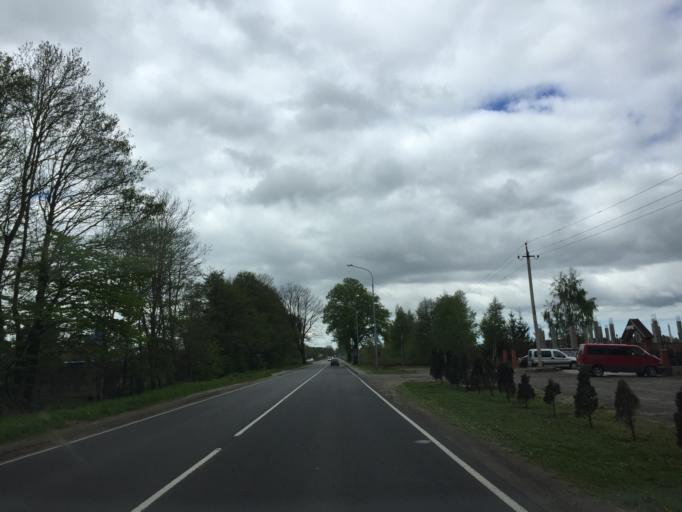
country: RU
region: Kaliningrad
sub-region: Gorod Kaliningrad
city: Kaliningrad
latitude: 54.6537
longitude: 20.3799
